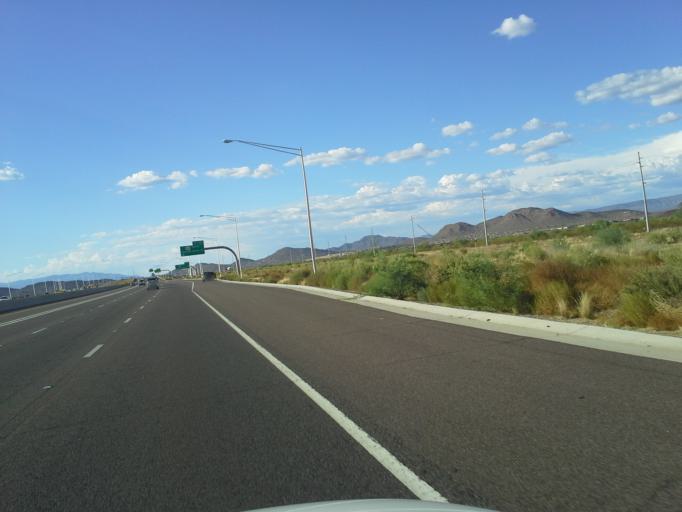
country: US
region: Arizona
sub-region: Maricopa County
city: Anthem
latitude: 33.7601
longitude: -112.1273
